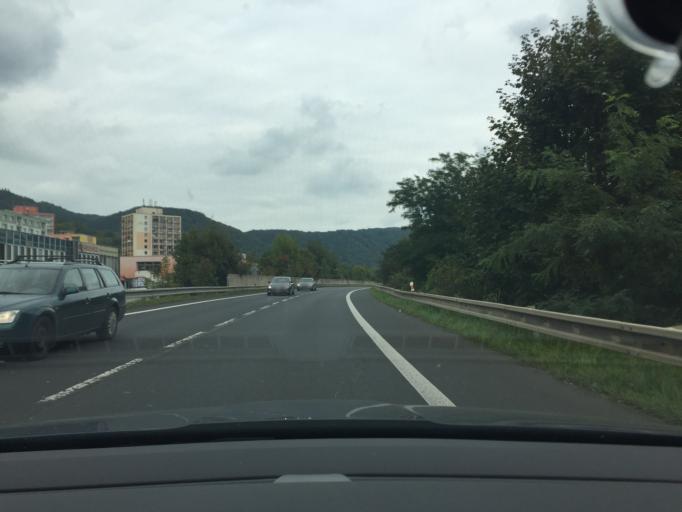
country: CZ
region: Ustecky
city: Velke Brezno
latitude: 50.6708
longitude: 14.1041
